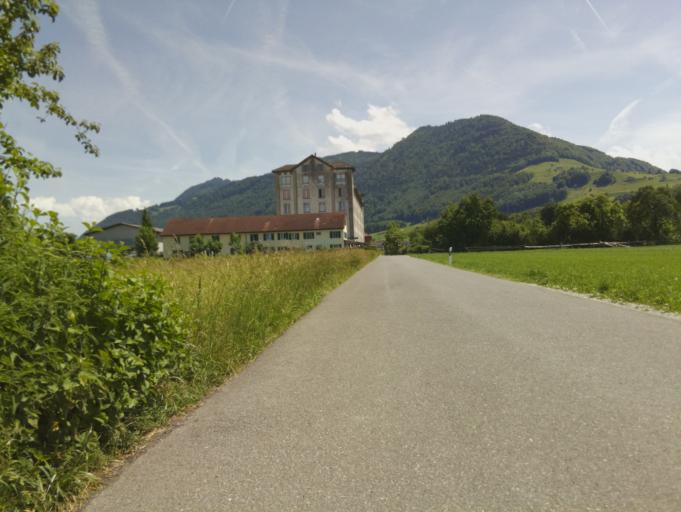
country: CH
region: Schwyz
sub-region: Bezirk March
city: Lachen
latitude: 47.1798
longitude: 8.8912
